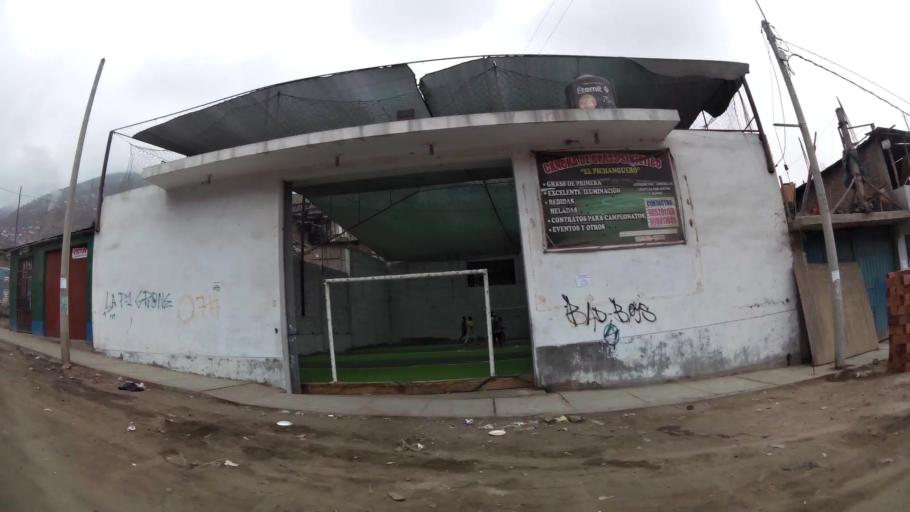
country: PE
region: Lima
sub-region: Lima
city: La Molina
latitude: -12.1277
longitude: -76.9520
